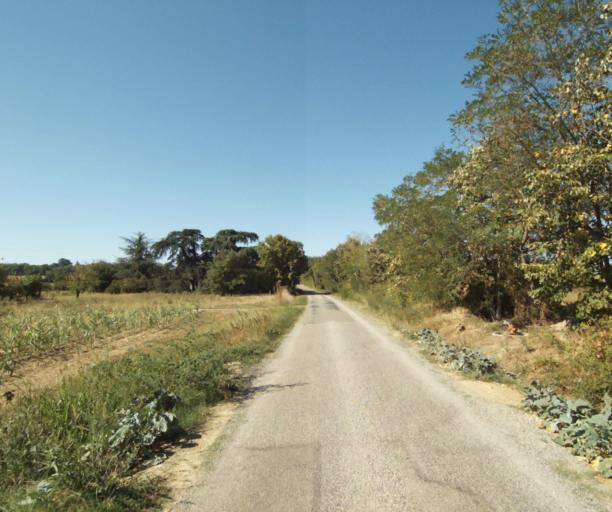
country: FR
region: Midi-Pyrenees
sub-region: Departement du Tarn-et-Garonne
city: Verdun-sur-Garonne
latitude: 43.8399
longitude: 1.2062
